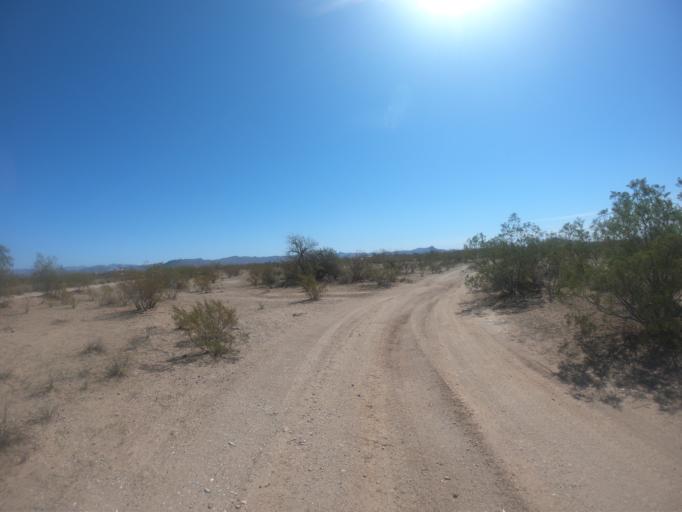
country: US
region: Arizona
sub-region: Pinal County
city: Gold Camp
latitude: 33.2392
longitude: -111.3391
